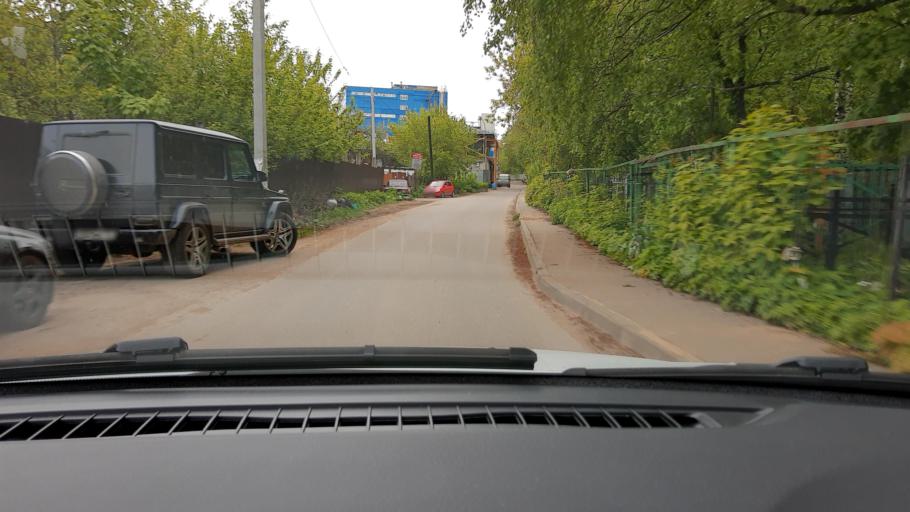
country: RU
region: Nizjnij Novgorod
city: Nizhniy Novgorod
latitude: 56.2806
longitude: 44.0012
